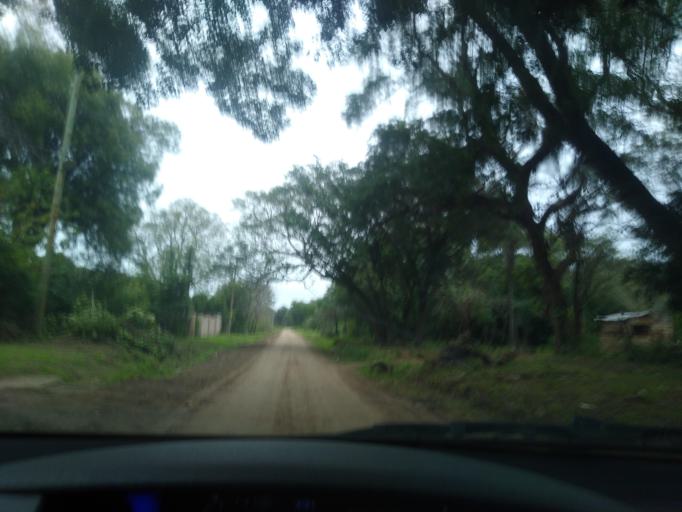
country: AR
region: Chaco
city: Colonia Benitez
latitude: -27.3317
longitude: -58.9581
